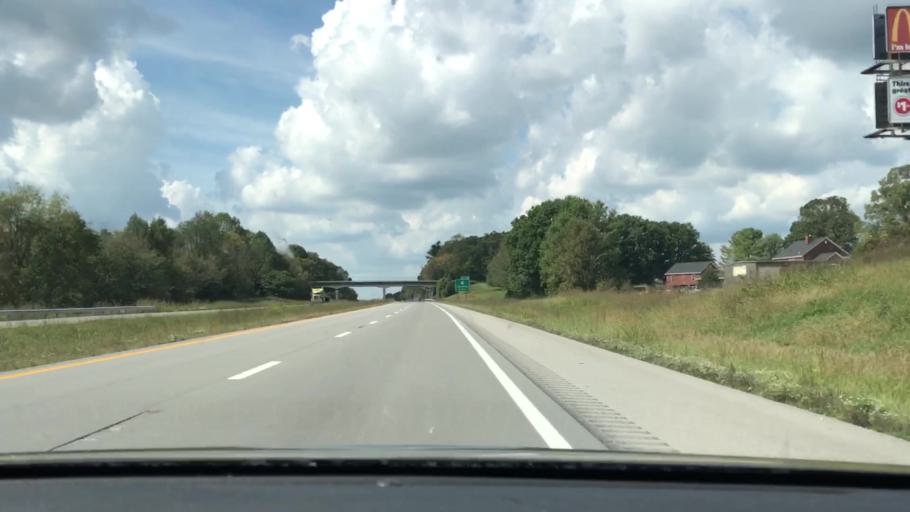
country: US
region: Kentucky
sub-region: Adair County
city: Columbia
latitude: 37.0863
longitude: -85.2624
